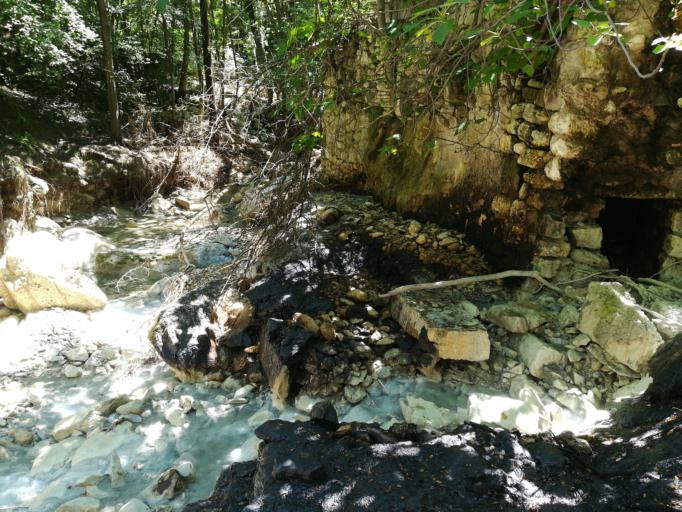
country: IT
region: Abruzzo
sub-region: Provincia di Pescara
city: Tocco da Casauria
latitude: 42.1906
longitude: 13.9155
